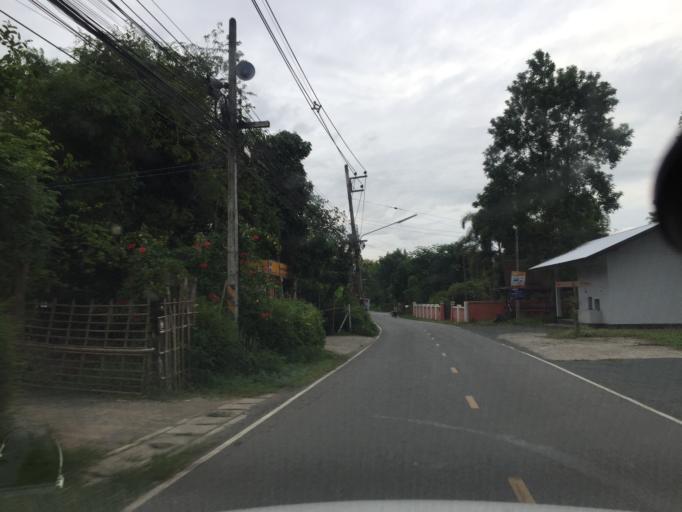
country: TH
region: Chiang Mai
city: Mae On
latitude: 18.8338
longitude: 99.1736
